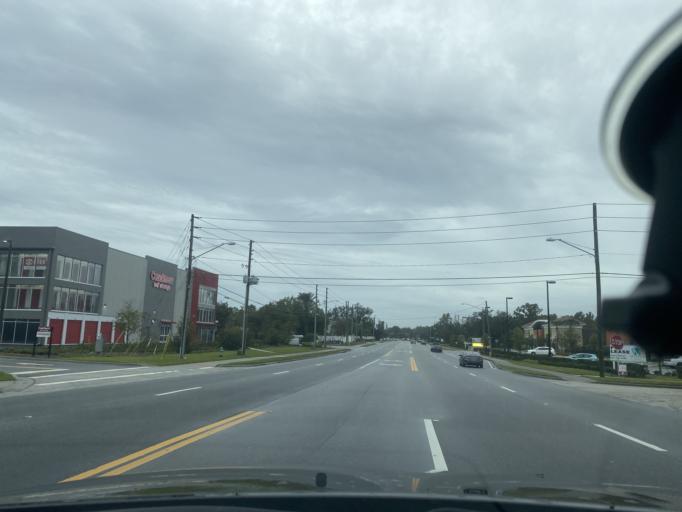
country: US
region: Florida
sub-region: Orange County
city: Alafaya
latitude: 28.5444
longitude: -81.2444
